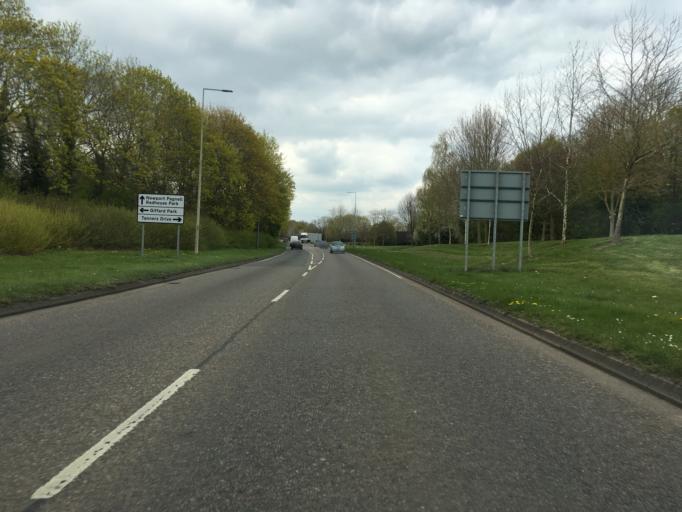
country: GB
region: England
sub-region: Milton Keynes
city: Newport Pagnell
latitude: 52.0745
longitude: -0.7448
